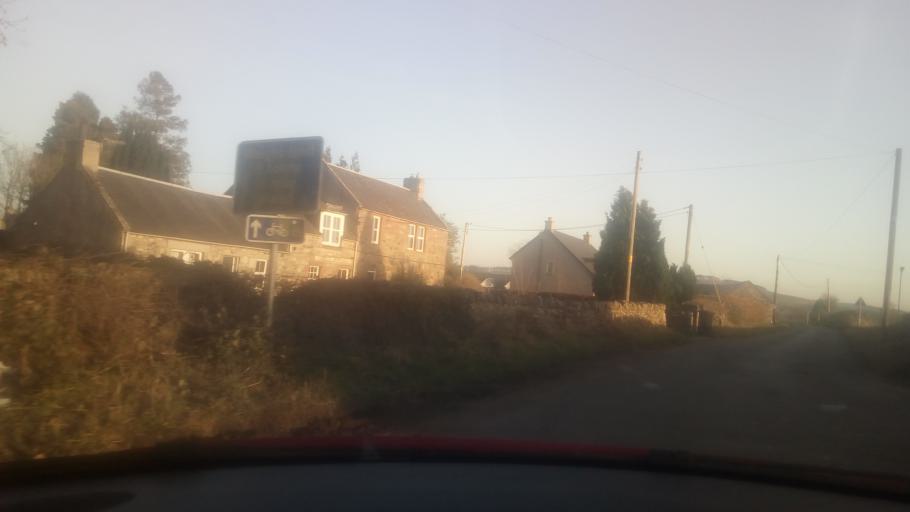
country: GB
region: Scotland
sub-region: The Scottish Borders
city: Jedburgh
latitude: 55.5241
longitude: -2.5199
